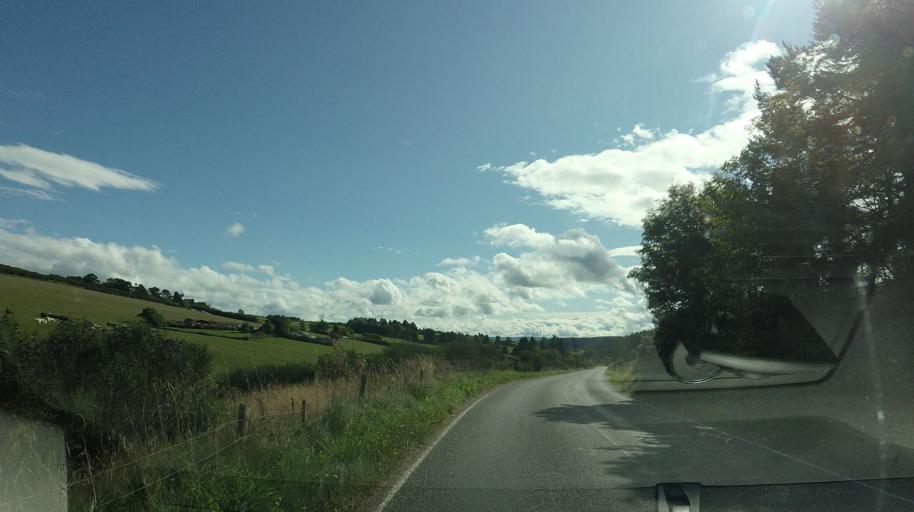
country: GB
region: Scotland
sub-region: Aberdeenshire
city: Alford
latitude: 57.1428
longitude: -2.7145
